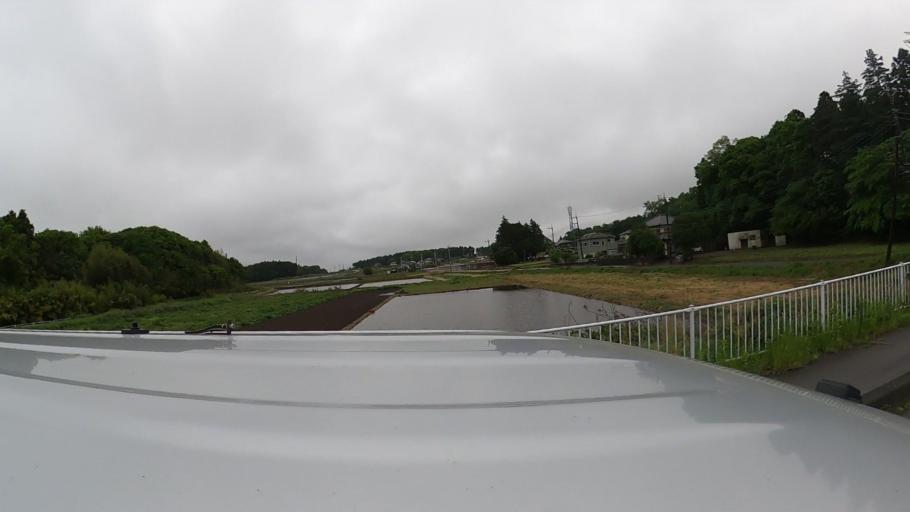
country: JP
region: Ibaraki
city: Ushiku
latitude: 36.0060
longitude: 140.1153
